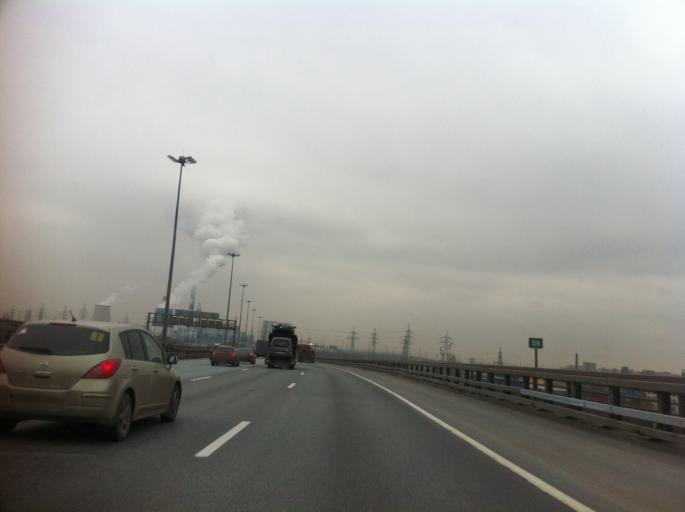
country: RU
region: St.-Petersburg
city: Obukhovo
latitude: 59.8461
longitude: 30.4583
